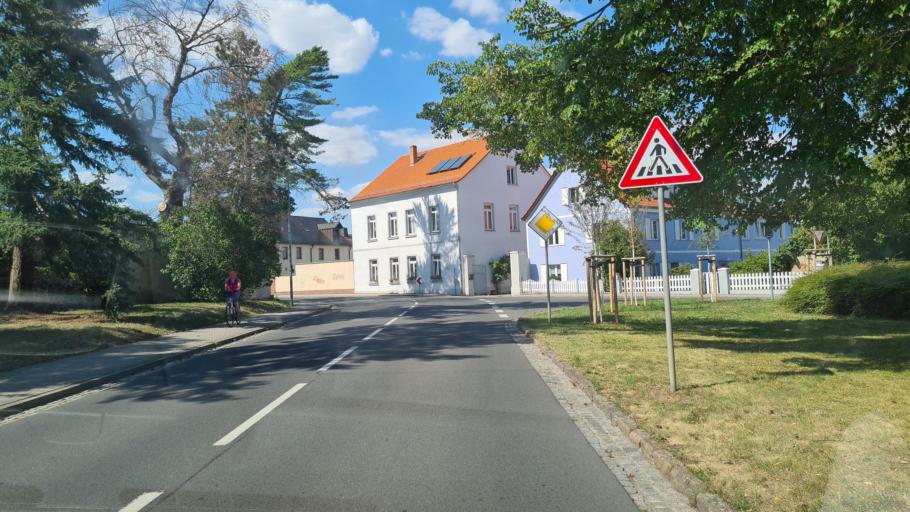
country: DE
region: Saxony
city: Machern
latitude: 51.3610
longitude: 12.6279
